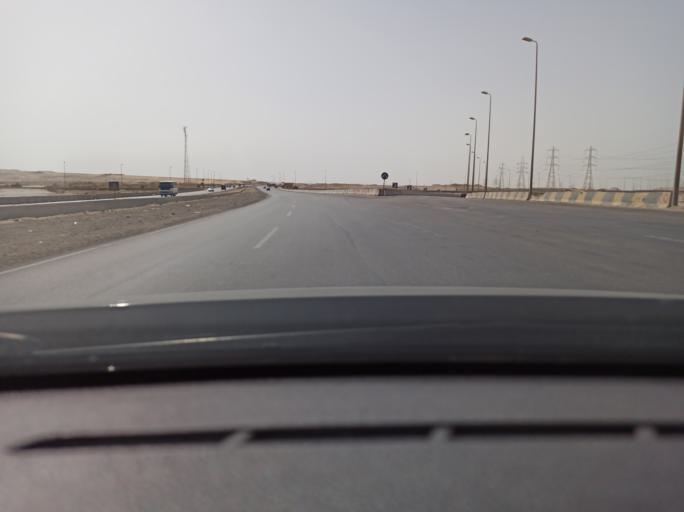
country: EG
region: Muhafazat al Qahirah
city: Halwan
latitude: 29.7215
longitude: 31.4052
